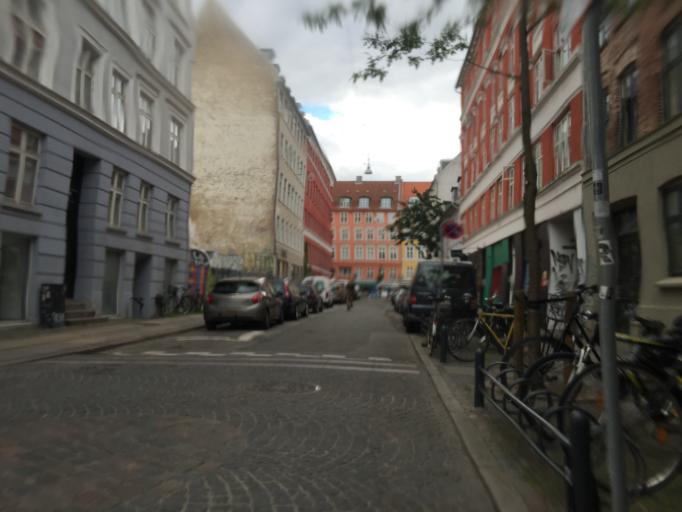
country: DK
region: Capital Region
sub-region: Frederiksberg Kommune
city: Frederiksberg
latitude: 55.6704
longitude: 12.5445
